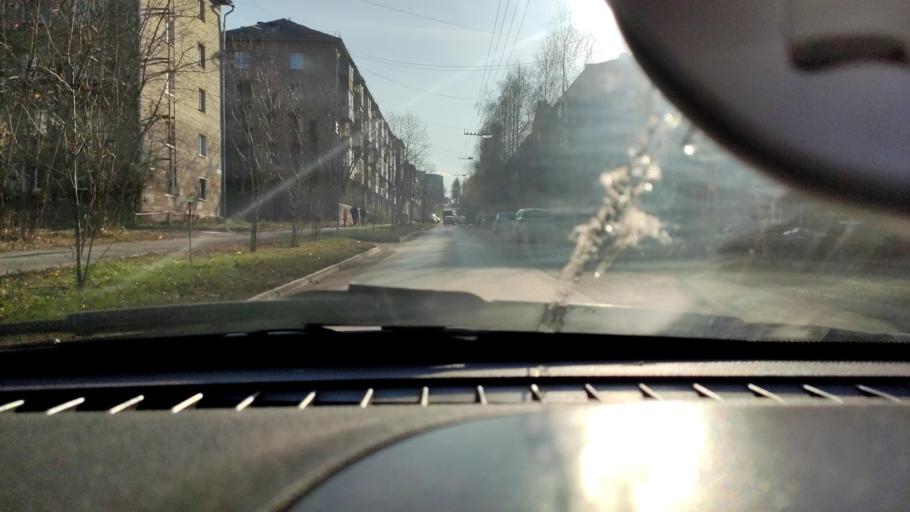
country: RU
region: Perm
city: Kondratovo
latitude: 57.9761
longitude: 56.1718
